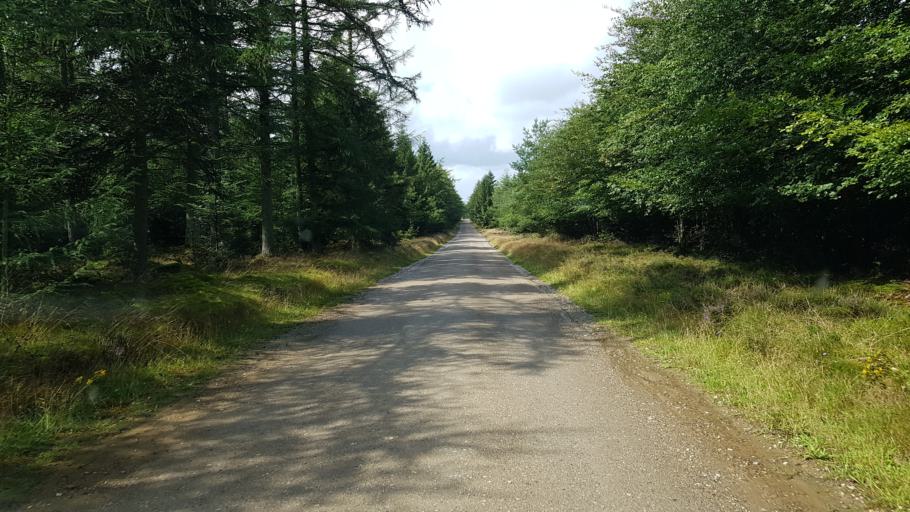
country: DK
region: South Denmark
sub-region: Vejen Kommune
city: Holsted
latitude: 55.5941
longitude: 8.9151
